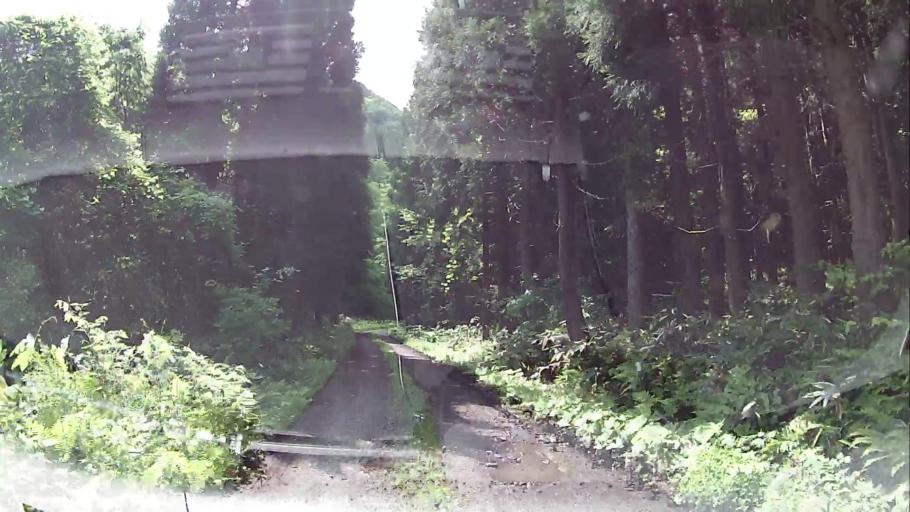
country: JP
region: Fukushima
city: Inawashiro
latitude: 37.3864
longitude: 140.0434
